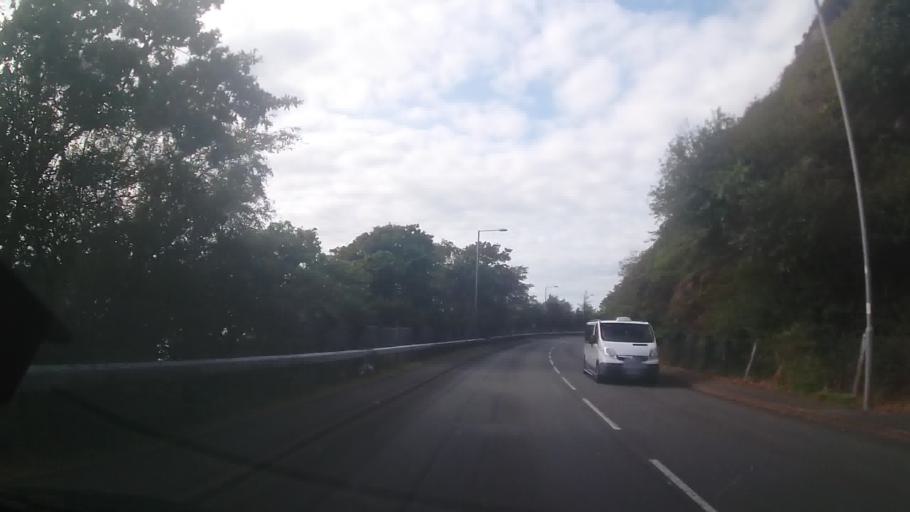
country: GB
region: Wales
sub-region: Gwynedd
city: Barmouth
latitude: 52.7316
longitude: -4.0645
